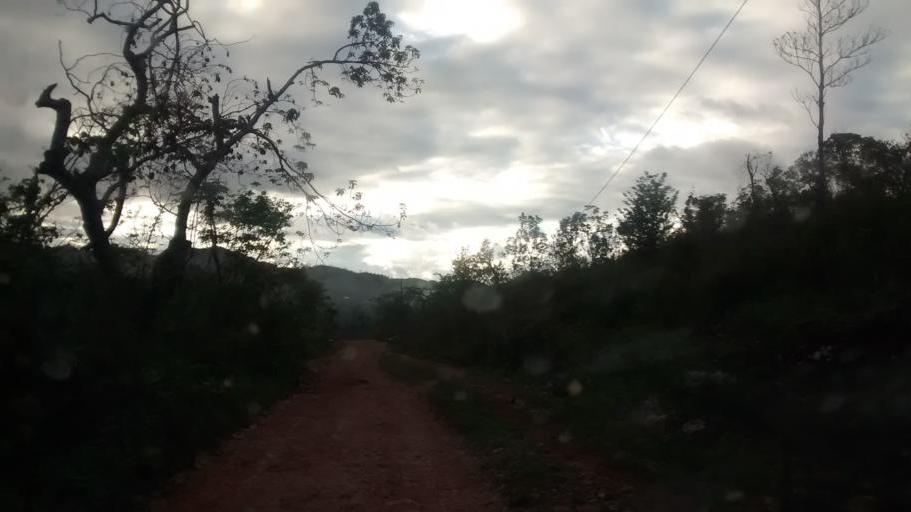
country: HT
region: Grandans
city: Corail
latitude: 18.4784
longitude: -73.8012
